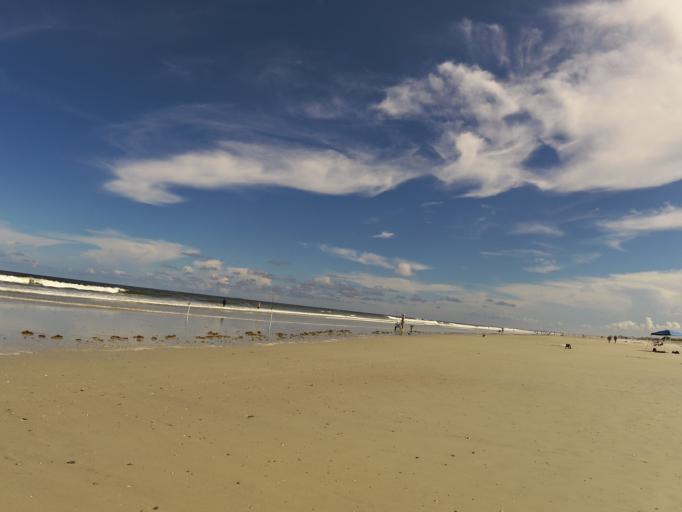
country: US
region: Florida
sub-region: Duval County
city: Atlantic Beach
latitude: 30.4621
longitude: -81.4112
